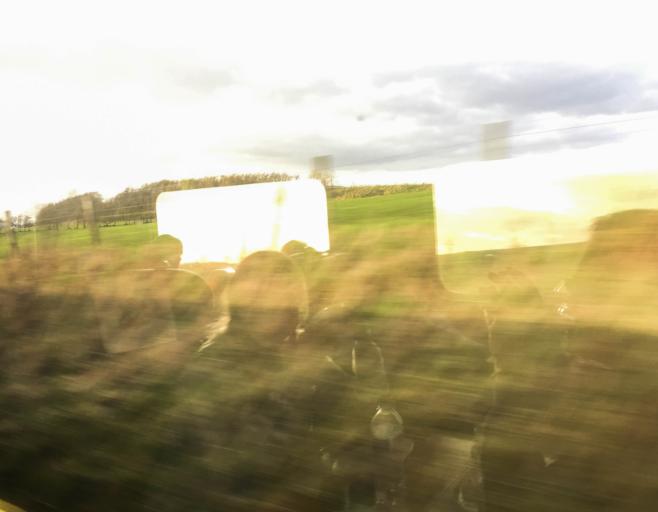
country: GB
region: Scotland
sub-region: Dumfries and Galloway
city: Annan
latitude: 55.0450
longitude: -3.2027
